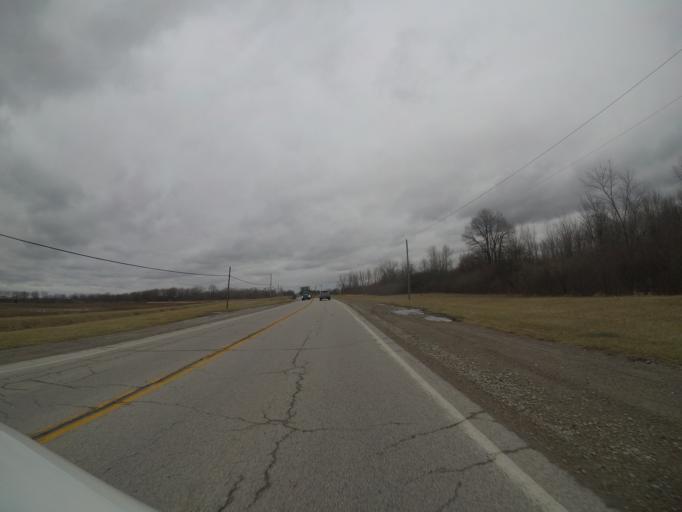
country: US
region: Ohio
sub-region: Wood County
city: Walbridge
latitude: 41.6015
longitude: -83.5123
